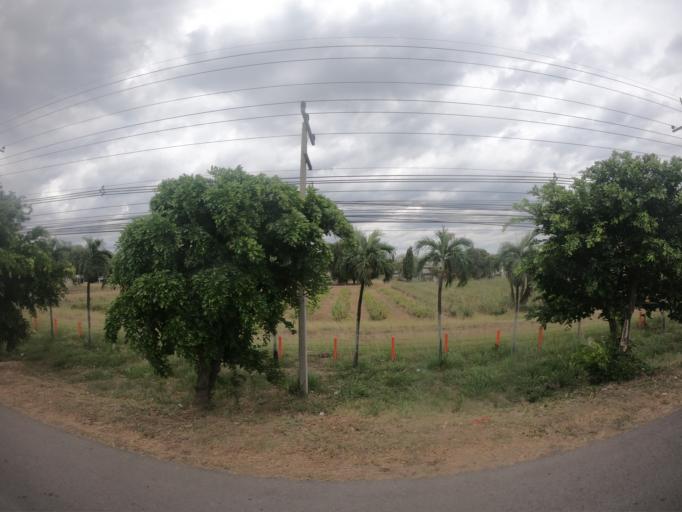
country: TH
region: Nakhon Ratchasima
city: Nakhon Ratchasima
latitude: 14.8742
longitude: 102.1784
